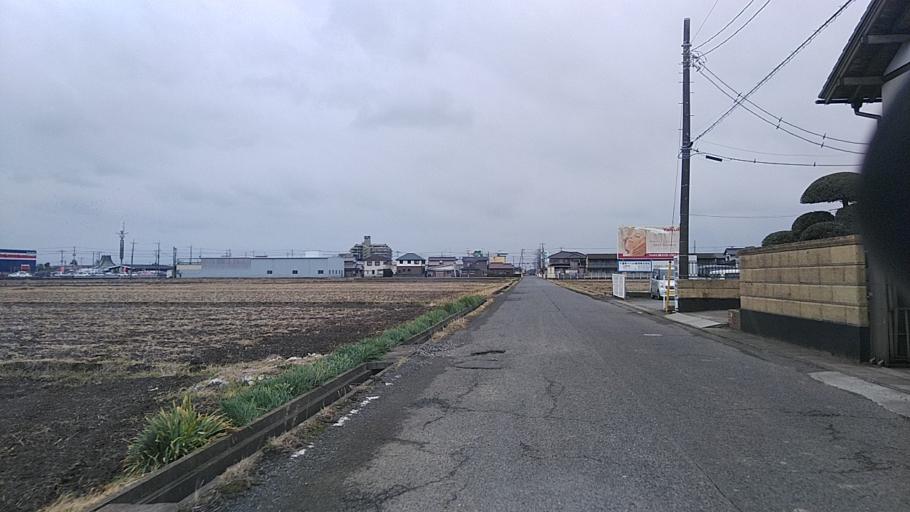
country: JP
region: Chiba
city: Togane
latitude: 35.5785
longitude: 140.3782
